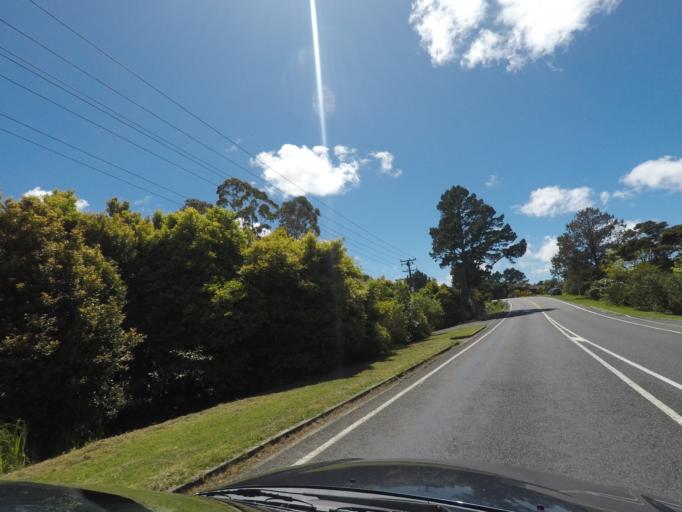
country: NZ
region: Auckland
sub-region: Auckland
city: Rothesay Bay
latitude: -36.7561
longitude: 174.6619
